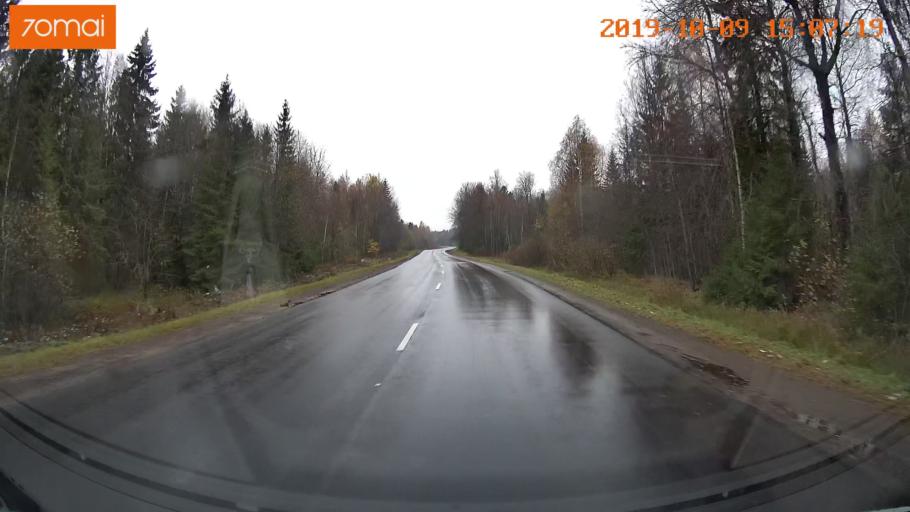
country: RU
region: Kostroma
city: Susanino
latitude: 58.2208
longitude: 41.6514
